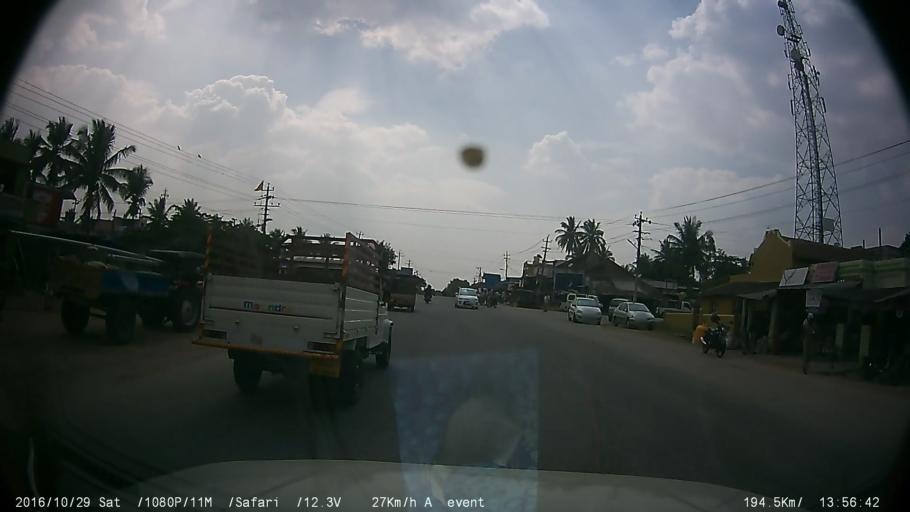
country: IN
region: Karnataka
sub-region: Mysore
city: Piriyapatna
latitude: 12.3373
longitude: 76.1596
